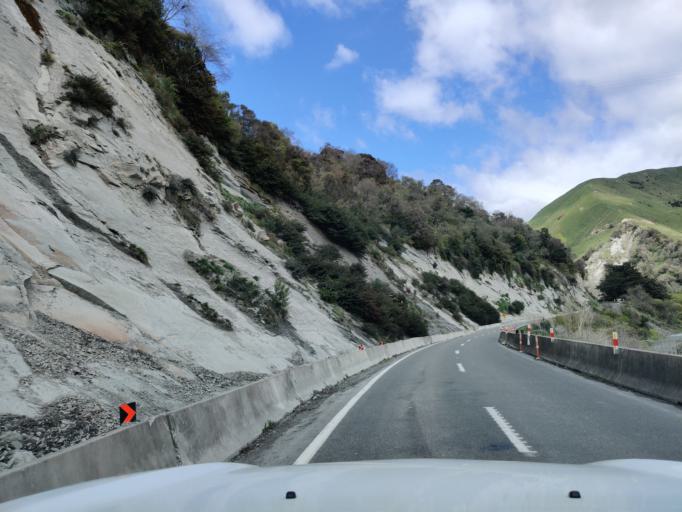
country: NZ
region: Manawatu-Wanganui
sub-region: Ruapehu District
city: Waiouru
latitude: -39.6454
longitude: 175.3267
